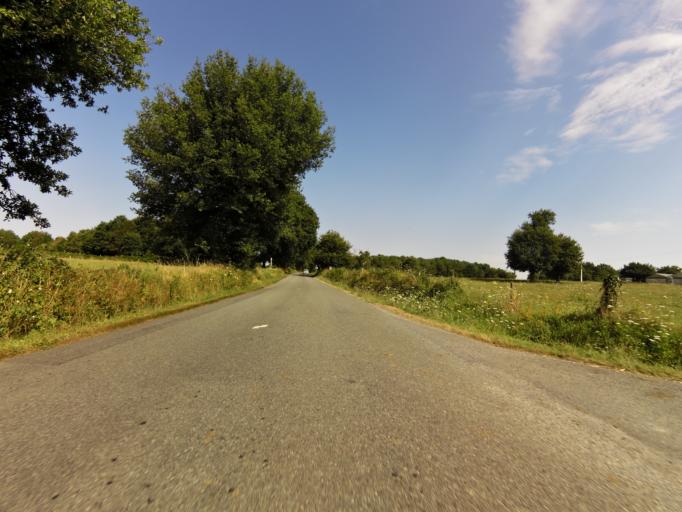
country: FR
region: Brittany
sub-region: Departement du Morbihan
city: Limerzel
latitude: 47.6445
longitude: -2.3710
